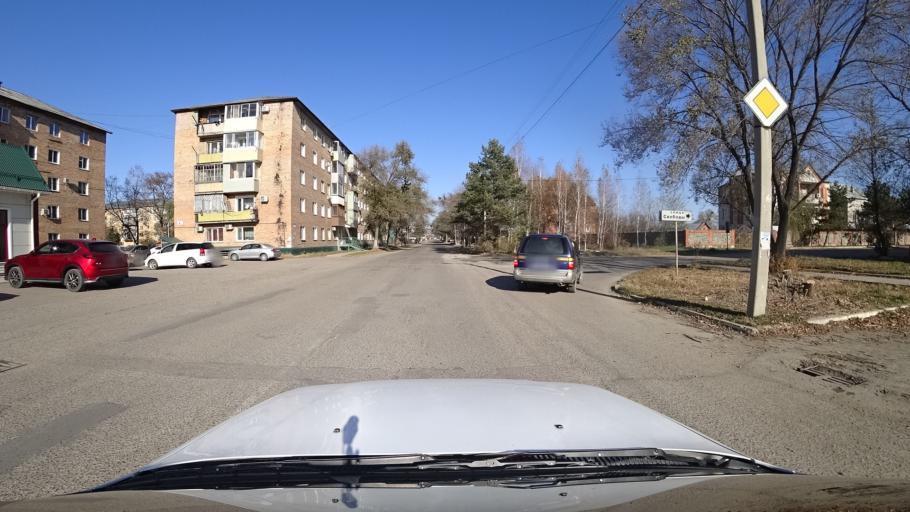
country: RU
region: Primorskiy
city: Dal'nerechensk
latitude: 45.9361
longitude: 133.7332
